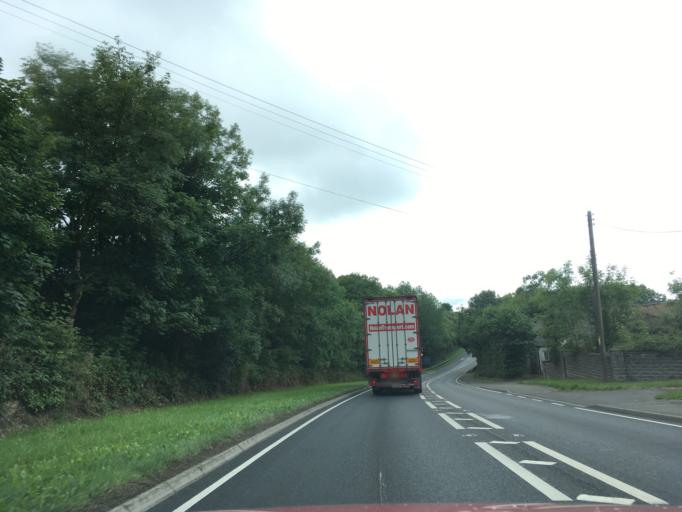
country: GB
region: Wales
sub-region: Pembrokeshire
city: Haverfordwest
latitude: 51.8049
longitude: -4.9490
